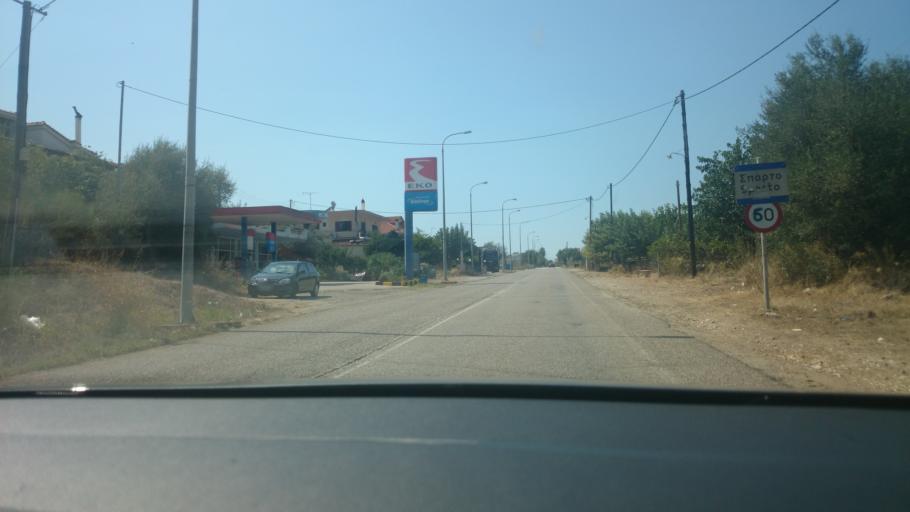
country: GR
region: West Greece
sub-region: Nomos Aitolias kai Akarnanias
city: Amfilochia
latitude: 38.9008
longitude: 21.1130
